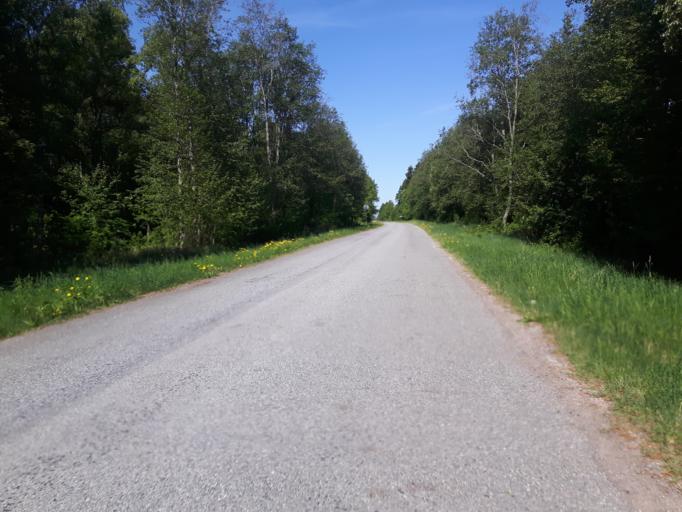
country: EE
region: Ida-Virumaa
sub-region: Aseri vald
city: Aseri
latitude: 59.4523
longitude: 26.8534
